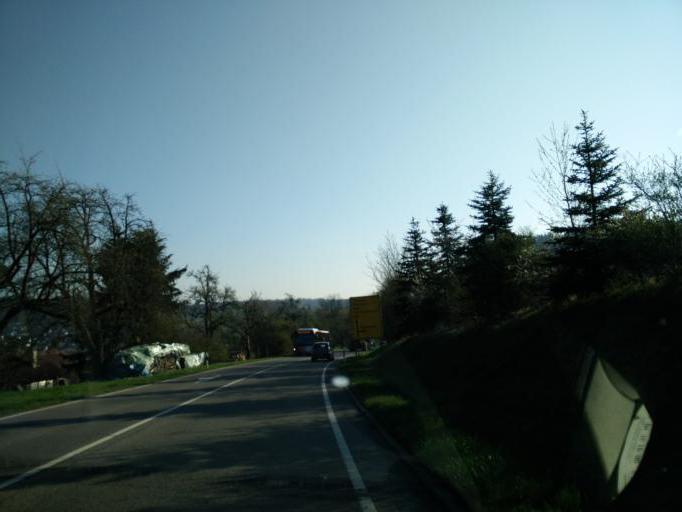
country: DE
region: Baden-Wuerttemberg
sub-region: Karlsruhe Region
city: Althengstett
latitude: 48.6918
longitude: 8.7744
